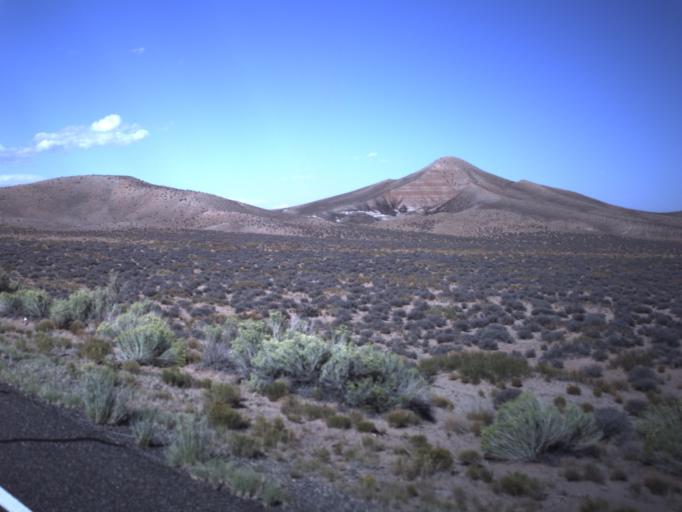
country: US
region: Utah
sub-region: Wayne County
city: Loa
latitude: 38.1102
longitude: -110.6246
